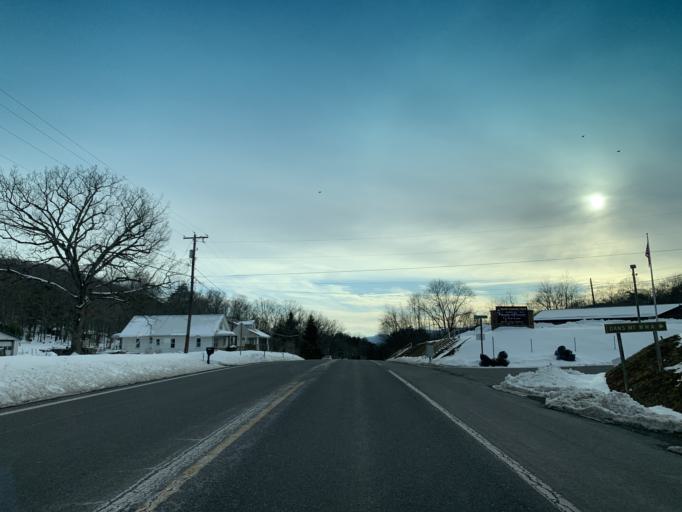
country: US
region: Maryland
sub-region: Allegany County
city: Lonaconing
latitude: 39.5062
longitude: -78.9275
